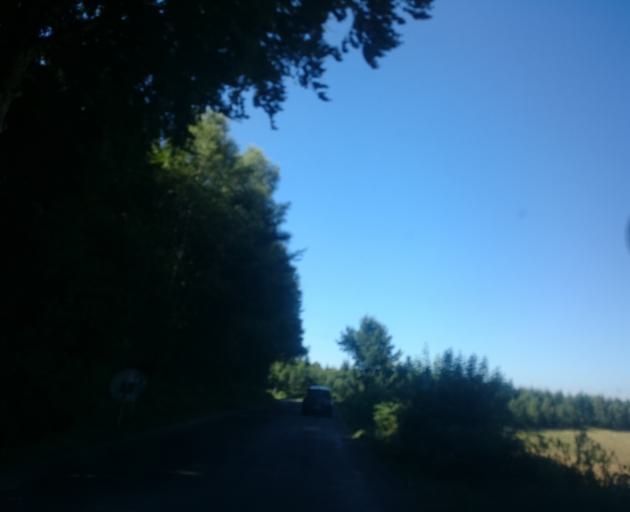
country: FR
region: Auvergne
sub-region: Departement du Cantal
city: Sansac-de-Marmiesse
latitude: 44.8166
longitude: 2.3705
